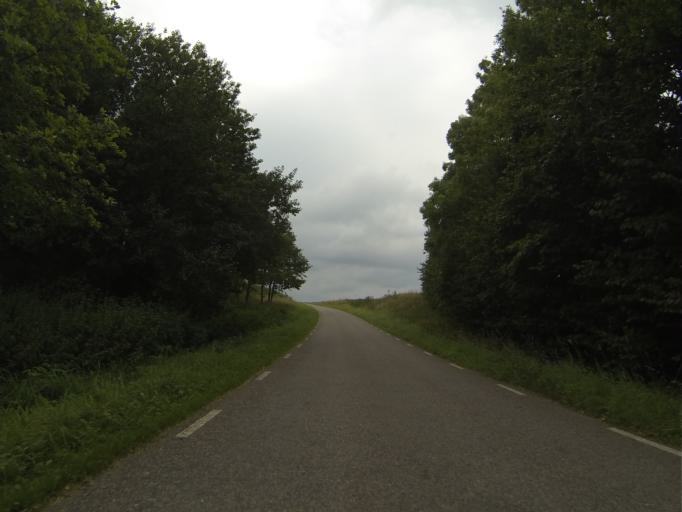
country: SE
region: Skane
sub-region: Eslovs Kommun
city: Eslov
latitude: 55.7606
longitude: 13.2634
